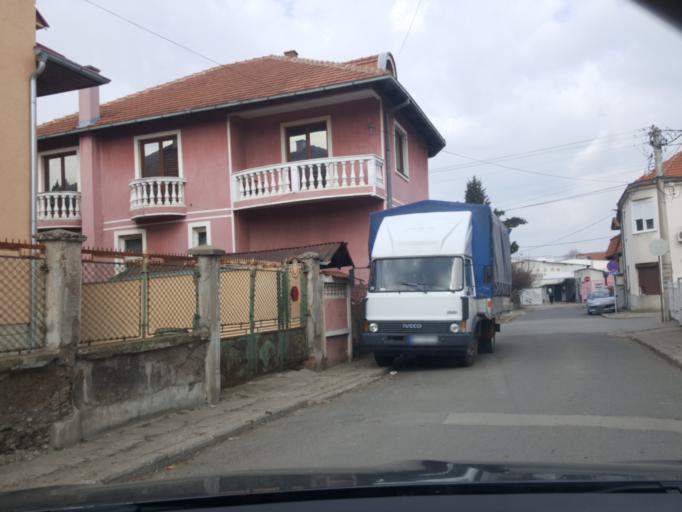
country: RS
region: Central Serbia
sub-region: Nisavski Okrug
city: Nis
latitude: 43.3136
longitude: 21.8758
